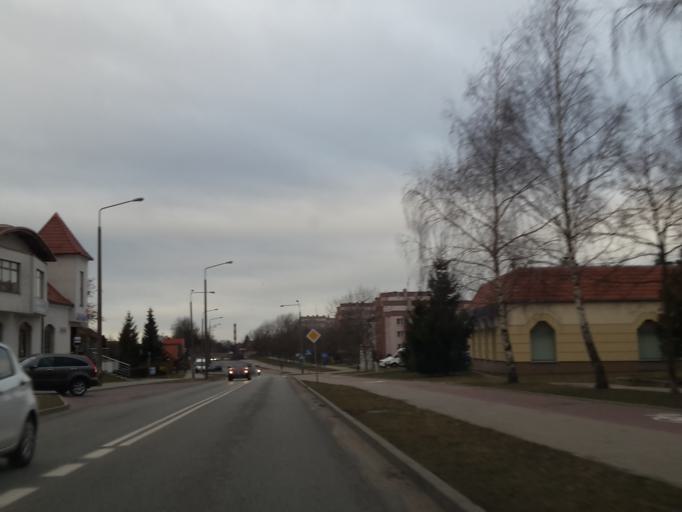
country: PL
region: Warmian-Masurian Voivodeship
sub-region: Powiat elblaski
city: Elblag
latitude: 54.1830
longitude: 19.4213
